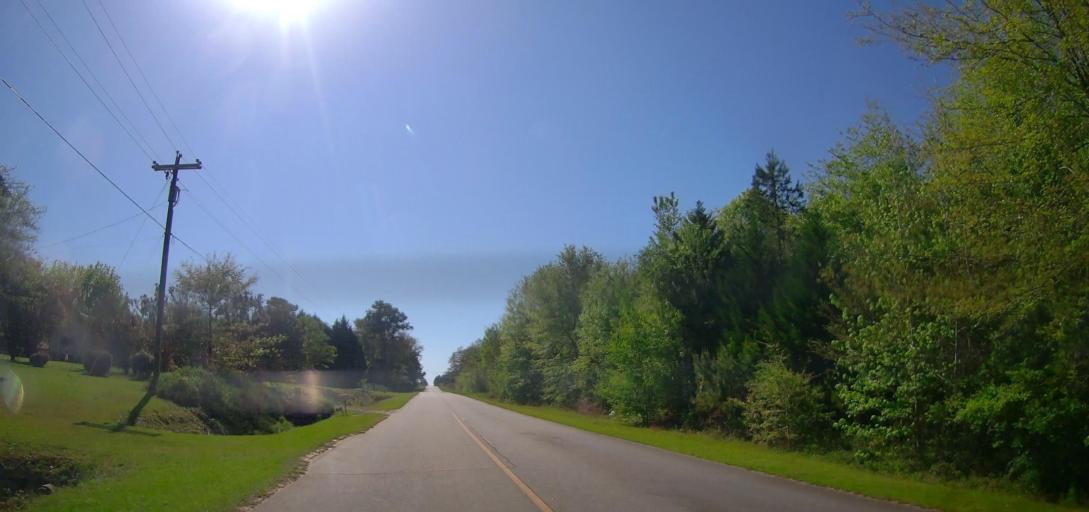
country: US
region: Georgia
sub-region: Pulaski County
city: Hawkinsville
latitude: 32.2404
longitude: -83.5147
